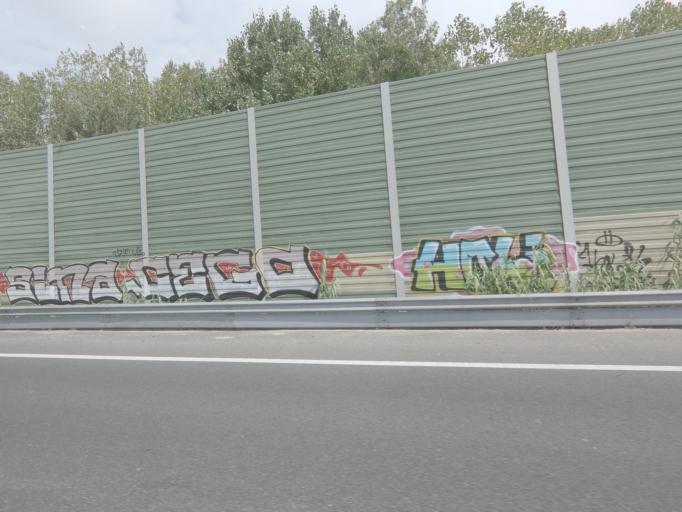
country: PT
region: Leiria
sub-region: Leiria
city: Leiria
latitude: 39.7503
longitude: -8.8177
